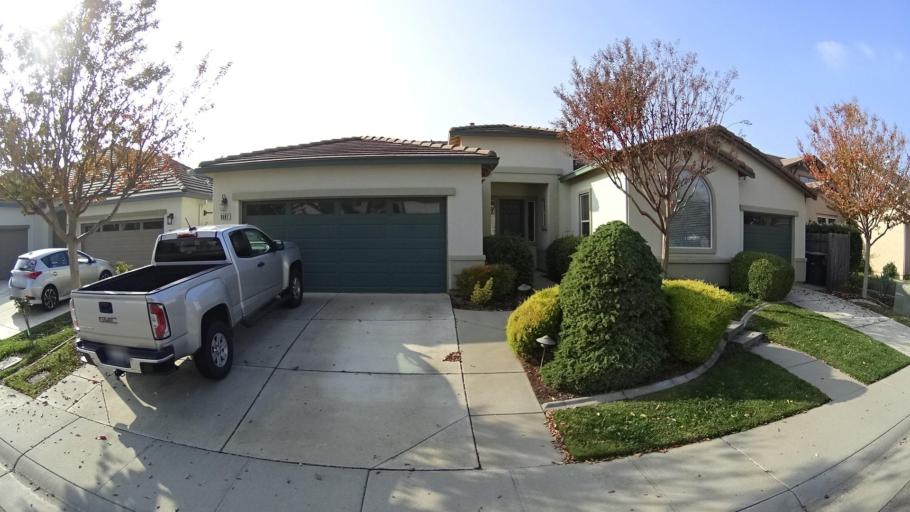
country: US
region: California
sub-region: Sacramento County
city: Elk Grove
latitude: 38.4149
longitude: -121.3365
